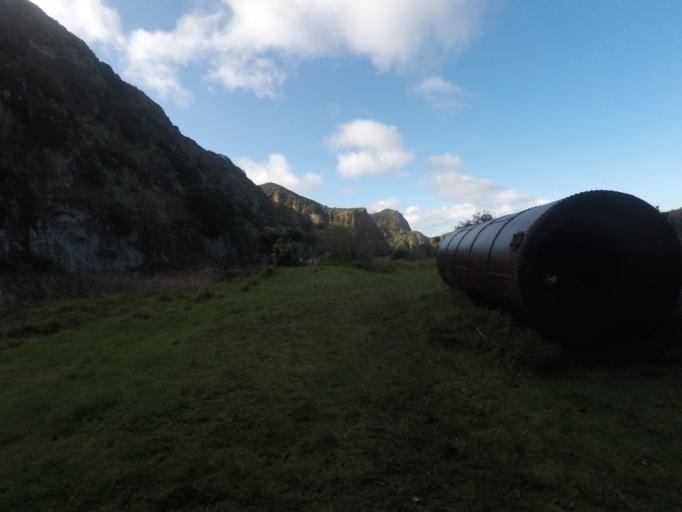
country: NZ
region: Auckland
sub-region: Auckland
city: Titirangi
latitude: -37.0034
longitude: 174.4811
